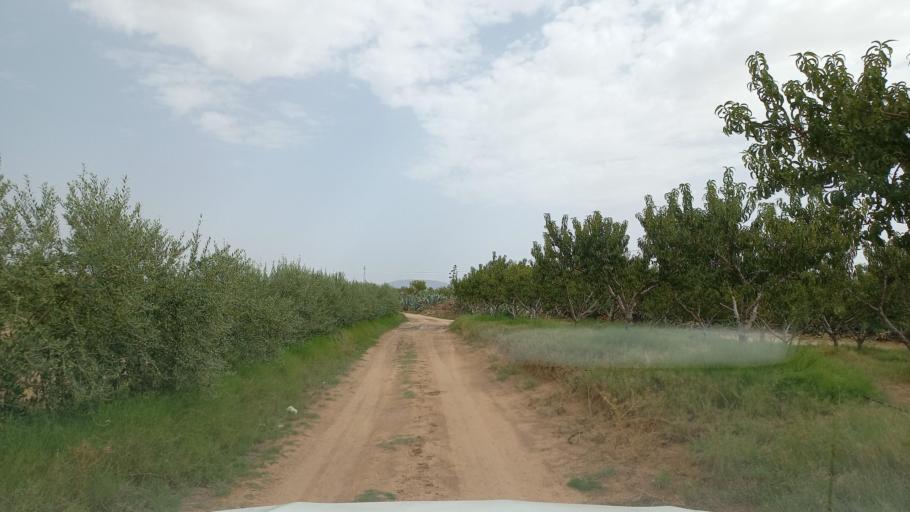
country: TN
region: Al Qasrayn
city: Kasserine
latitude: 35.2848
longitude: 9.0232
